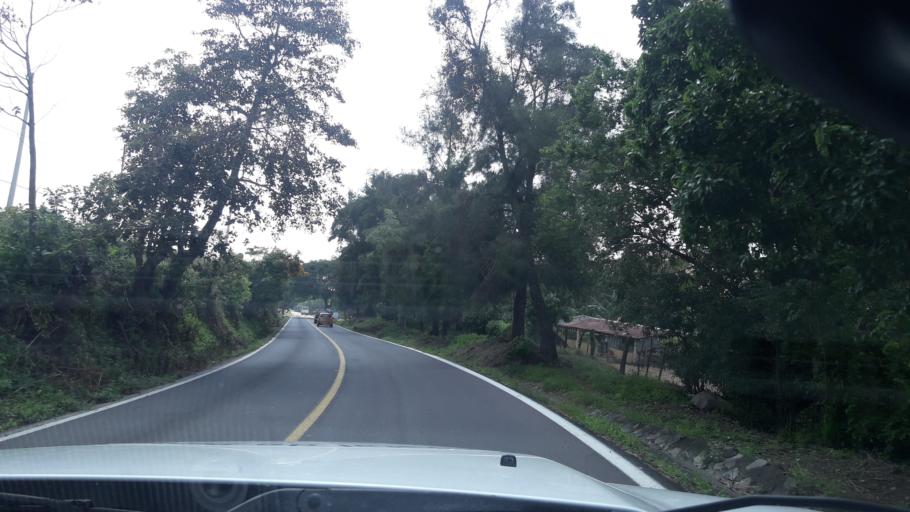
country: MX
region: Colima
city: Suchitlan
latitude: 19.3963
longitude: -103.7034
